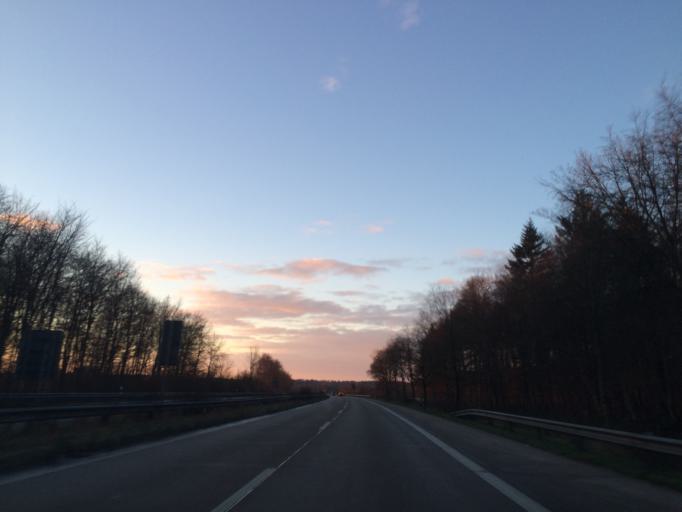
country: DE
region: Schleswig-Holstein
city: Susel
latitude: 54.0521
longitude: 10.7335
